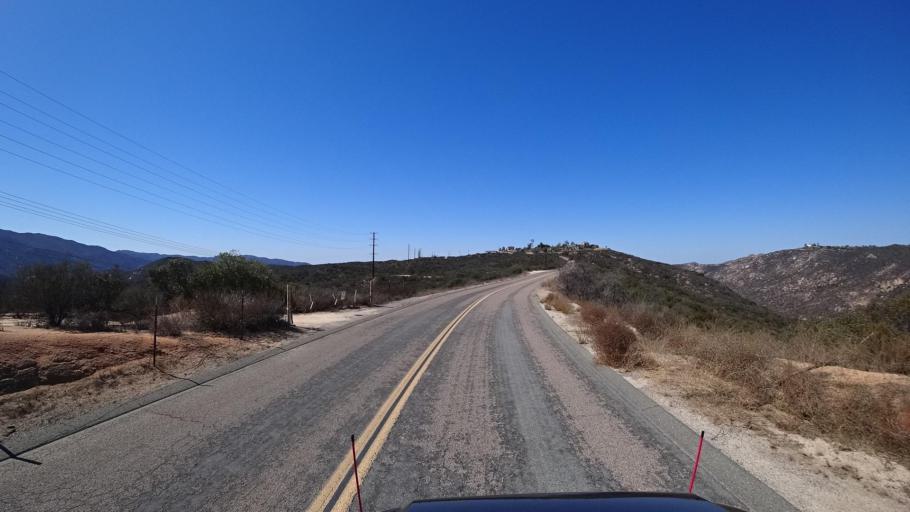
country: US
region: California
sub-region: San Diego County
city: Alpine
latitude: 32.7978
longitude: -116.7818
